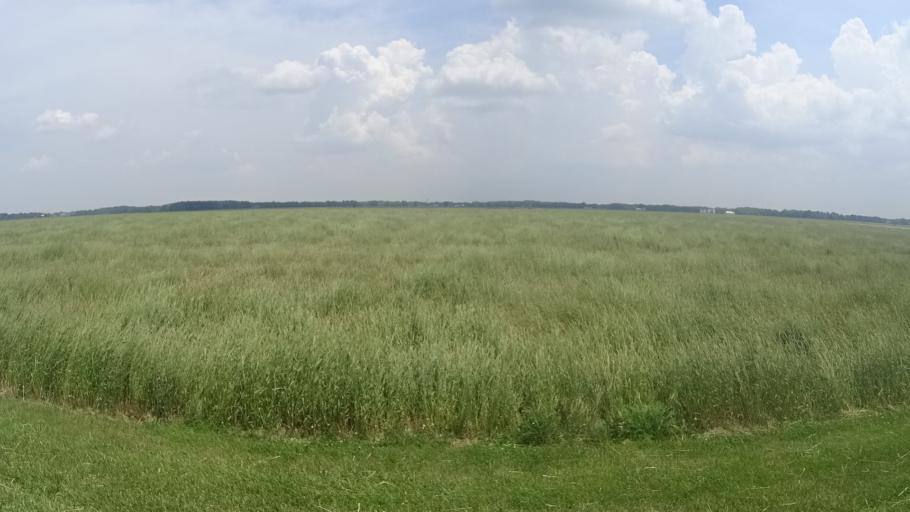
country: US
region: Ohio
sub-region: Huron County
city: Monroeville
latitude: 41.2943
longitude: -82.6923
